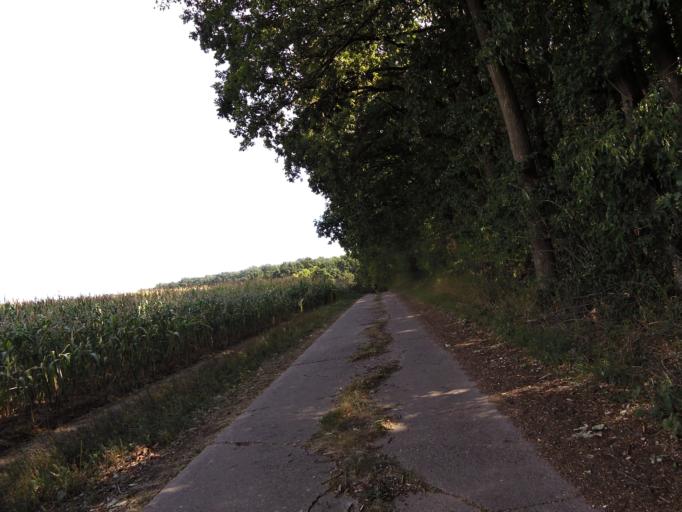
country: DE
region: Bavaria
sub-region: Regierungsbezirk Unterfranken
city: Theilheim
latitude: 49.7487
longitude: 10.0230
